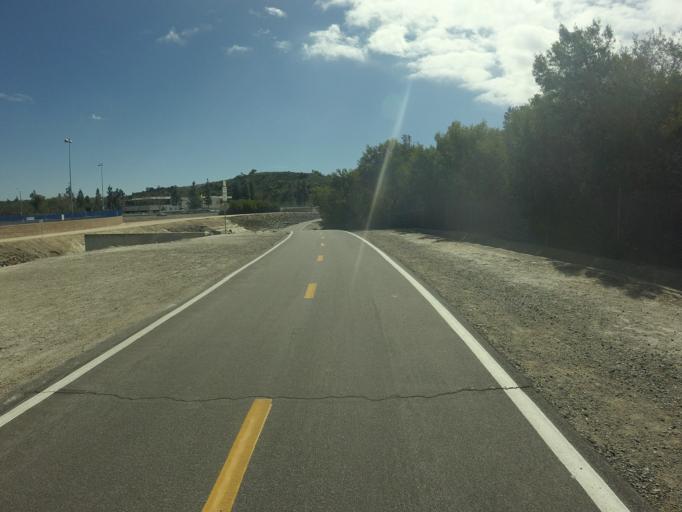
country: US
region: California
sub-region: Orange County
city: Aliso Viejo
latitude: 33.5583
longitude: -117.7183
